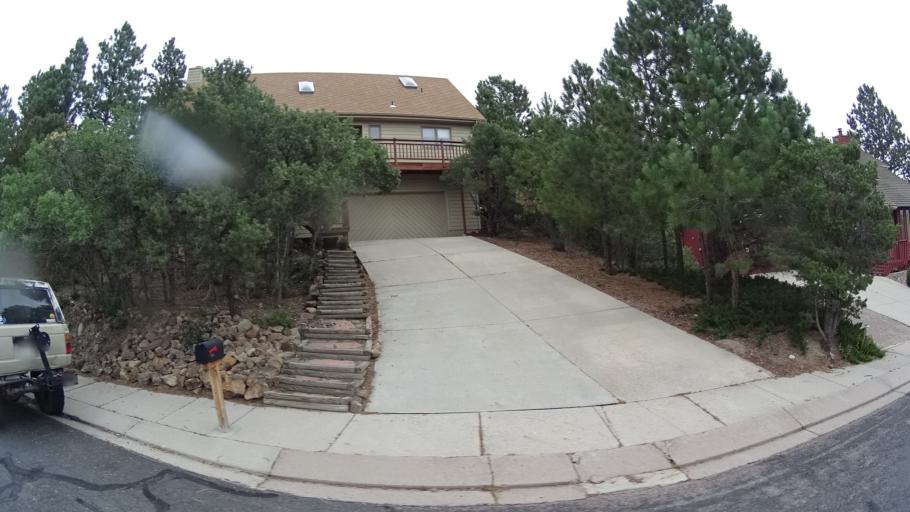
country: US
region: Colorado
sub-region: El Paso County
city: Colorado Springs
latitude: 38.9199
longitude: -104.8087
